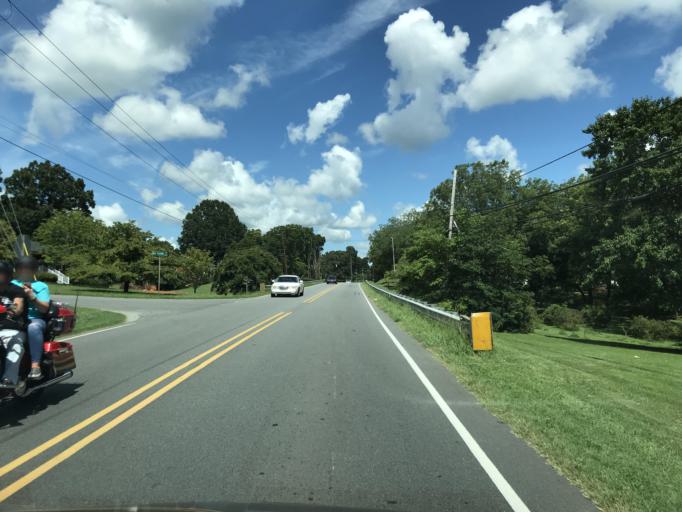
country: US
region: North Carolina
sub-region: Lincoln County
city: Pumpkin Center
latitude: 35.5006
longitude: -81.1868
